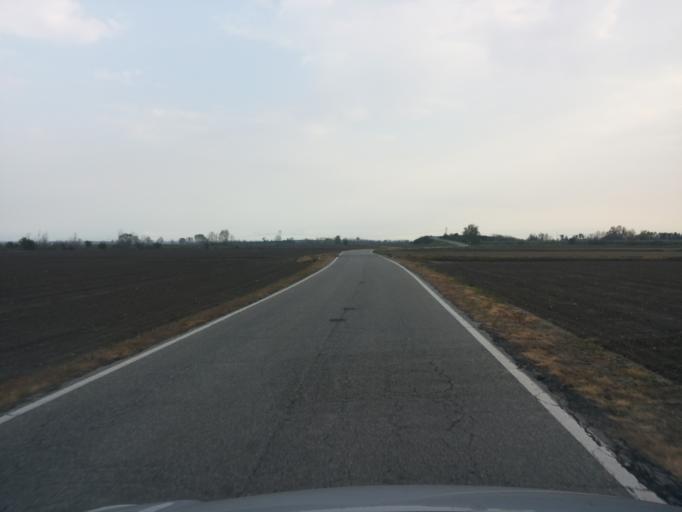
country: IT
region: Piedmont
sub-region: Provincia di Alessandria
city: Villanova Monferrato
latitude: 45.1978
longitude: 8.4962
